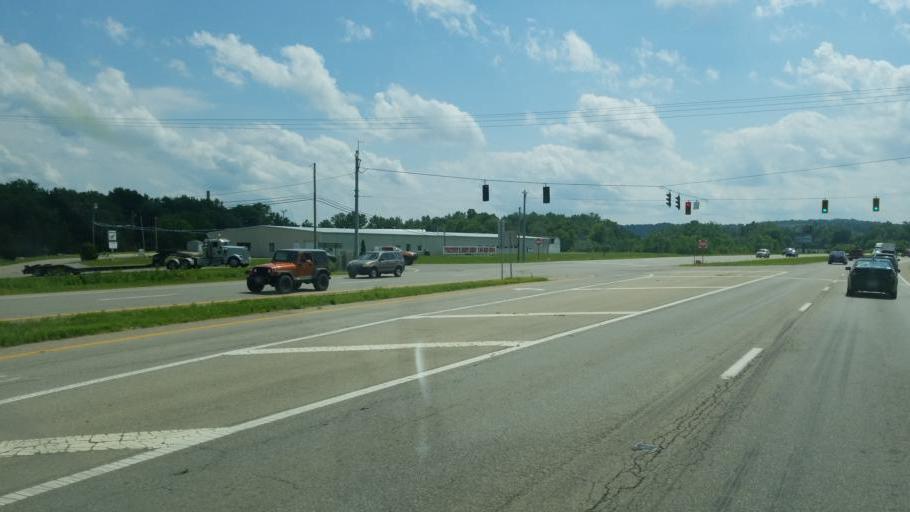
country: US
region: Ohio
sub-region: Coshocton County
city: Coshocton
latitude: 40.2876
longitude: -81.8635
